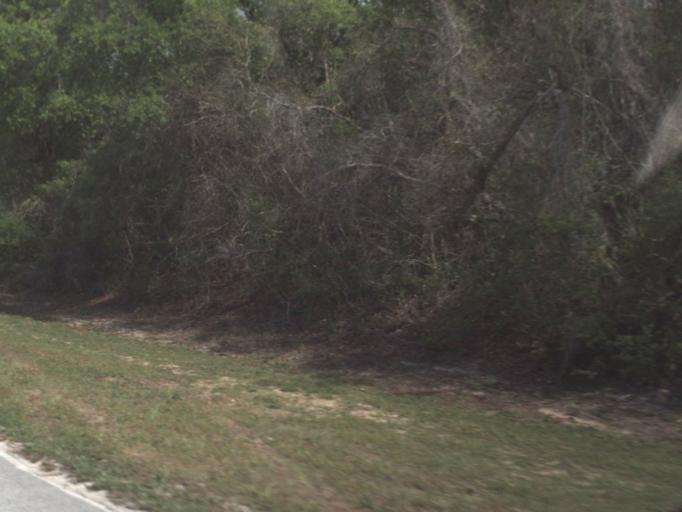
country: US
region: Florida
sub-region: Lake County
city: Astor
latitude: 29.2885
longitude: -81.6541
